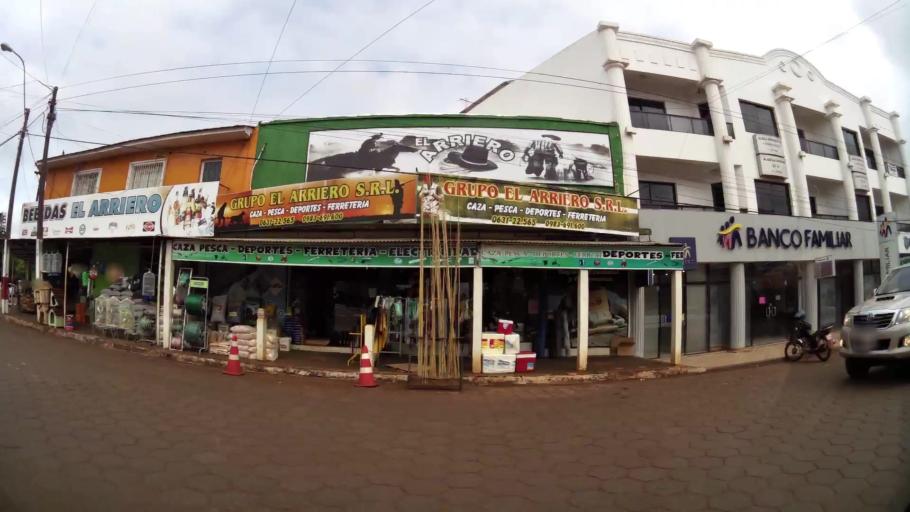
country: PY
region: Alto Parana
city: Ciudad del Este
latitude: -25.3956
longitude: -54.6389
